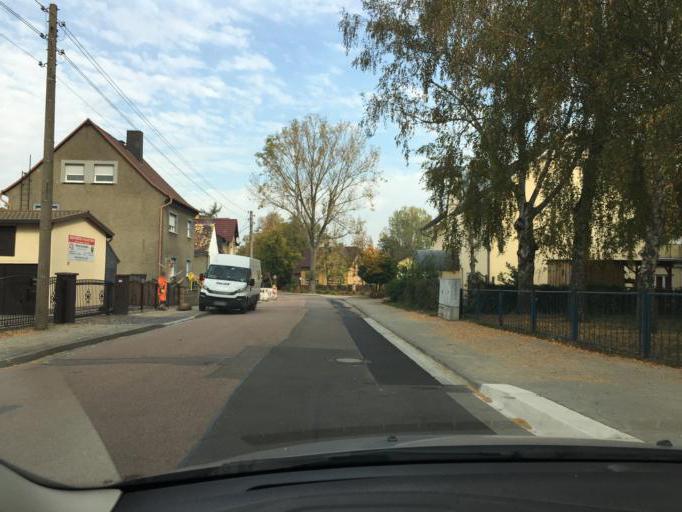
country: DE
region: Saxony
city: Zwochau
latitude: 51.4630
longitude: 12.2701
